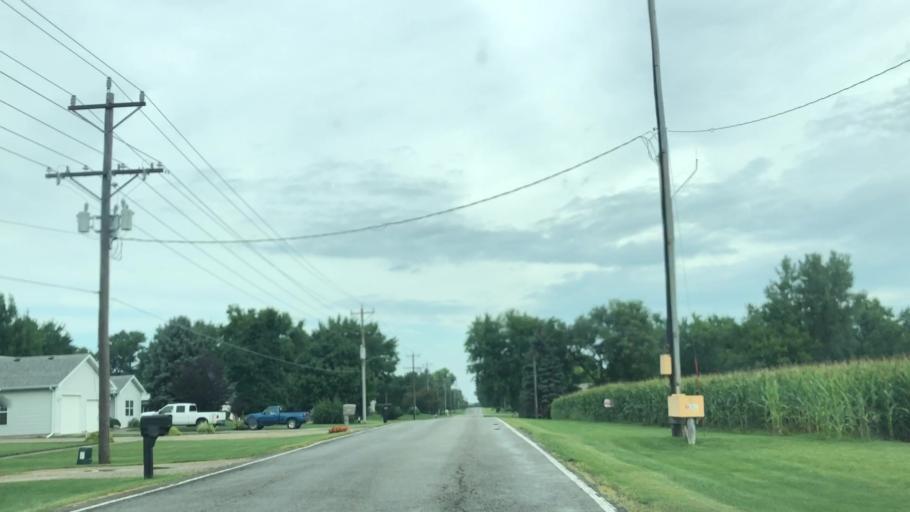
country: US
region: Iowa
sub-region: Marshall County
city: Marshalltown
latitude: 42.0397
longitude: -92.9610
